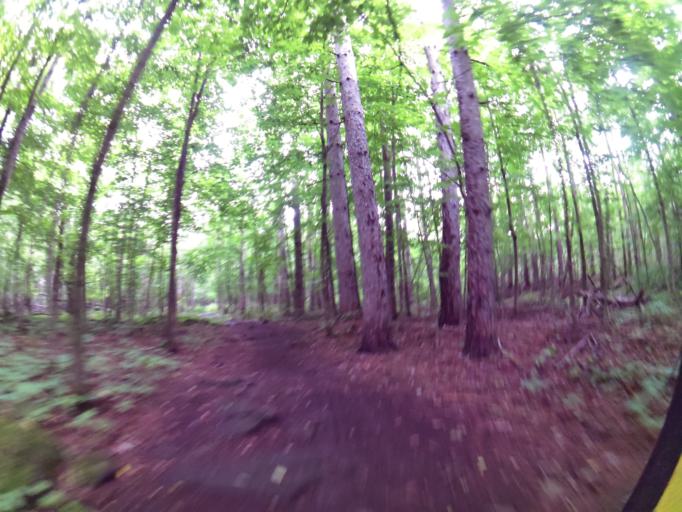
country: CA
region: Ontario
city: Bells Corners
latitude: 45.2989
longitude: -75.8444
